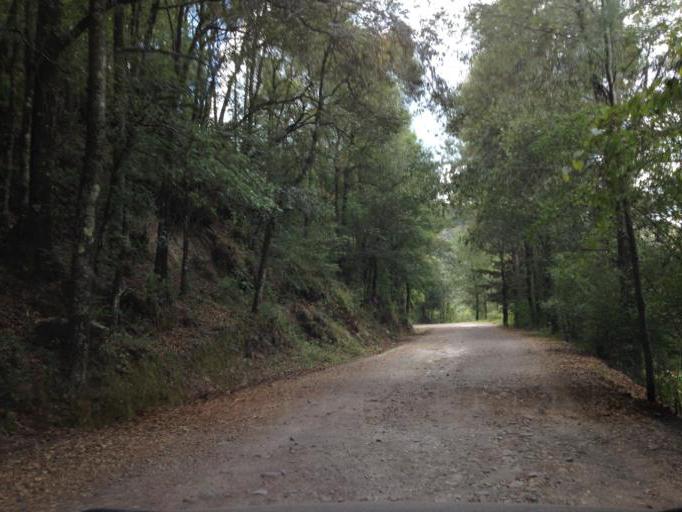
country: MX
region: Hidalgo
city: Mineral del Monte
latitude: 20.2053
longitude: -98.6641
